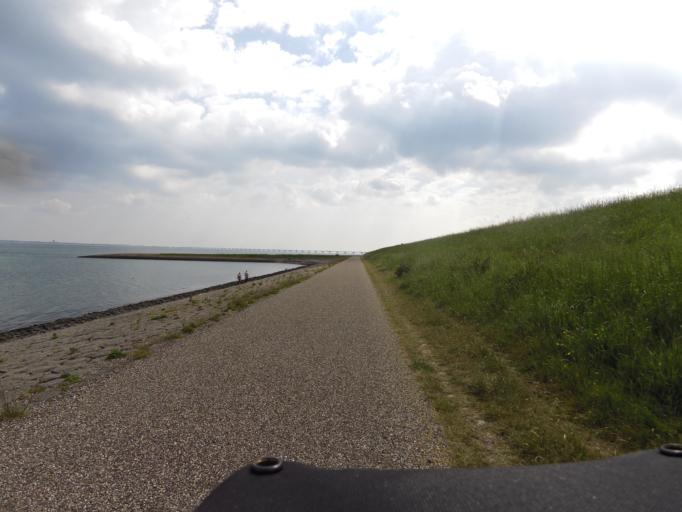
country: NL
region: Zeeland
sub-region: Gemeente Goes
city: Goes
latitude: 51.6049
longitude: 3.8371
